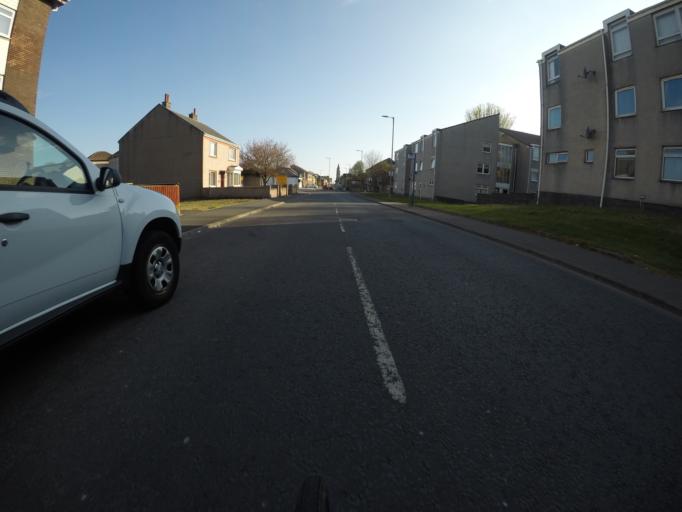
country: GB
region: Scotland
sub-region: North Ayrshire
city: Saltcoats
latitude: 55.6360
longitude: -4.7837
